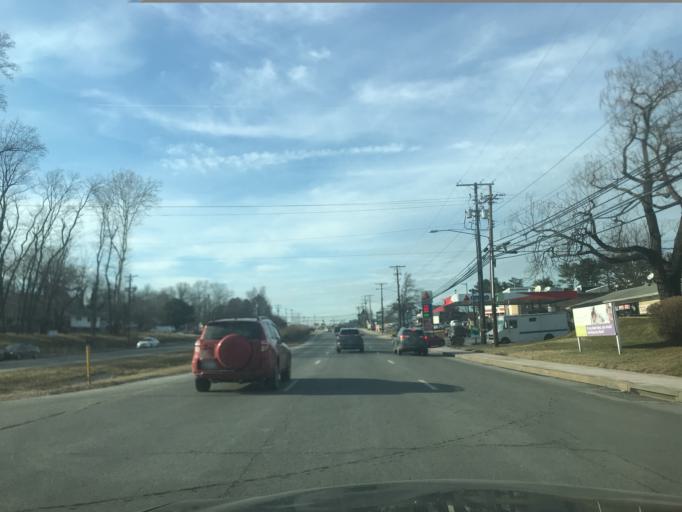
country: US
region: Maryland
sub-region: Montgomery County
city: Aspen Hill
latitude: 39.0782
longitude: -77.0715
